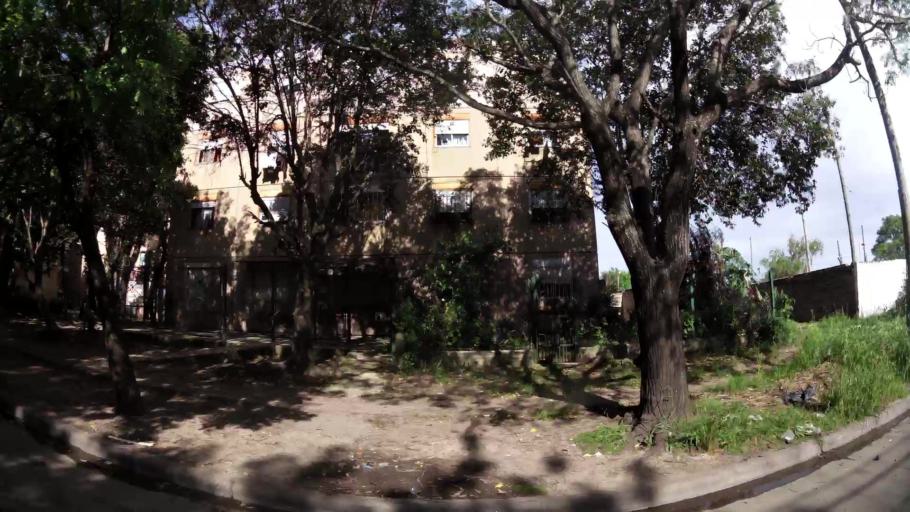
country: AR
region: Buenos Aires
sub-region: Partido de Almirante Brown
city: Adrogue
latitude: -34.8211
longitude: -58.3473
